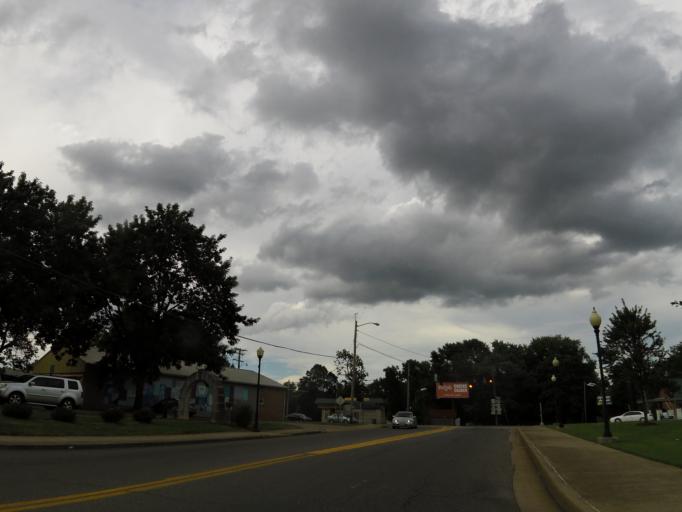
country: US
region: Kentucky
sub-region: Christian County
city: Hopkinsville
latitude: 36.8676
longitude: -87.4934
